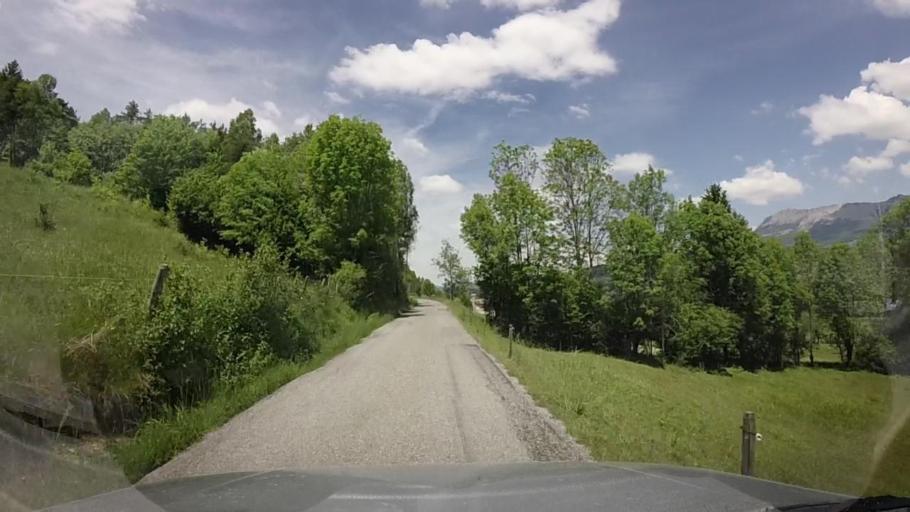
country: FR
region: Provence-Alpes-Cote d'Azur
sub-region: Departement des Alpes-de-Haute-Provence
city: Seyne-les-Alpes
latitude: 44.3324
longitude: 6.3491
